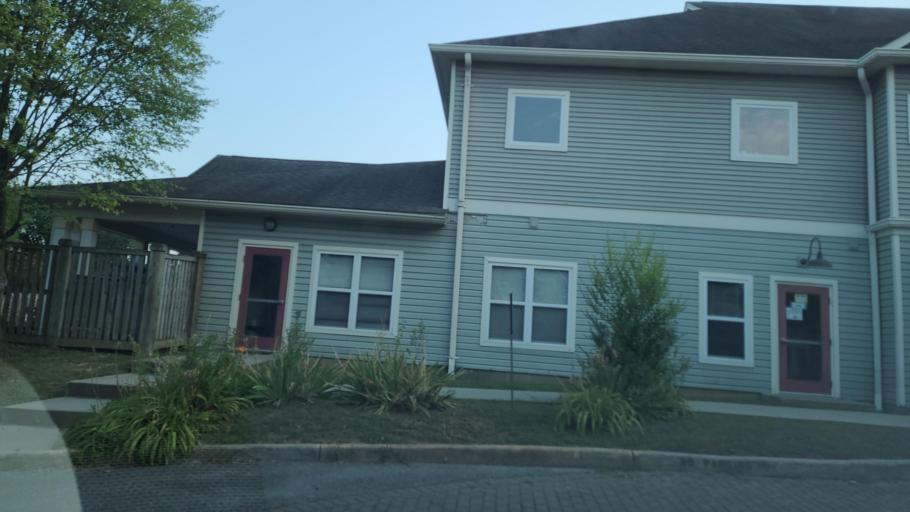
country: US
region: Virginia
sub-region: City of Roanoke
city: Roanoke
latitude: 37.2773
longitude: -79.9550
